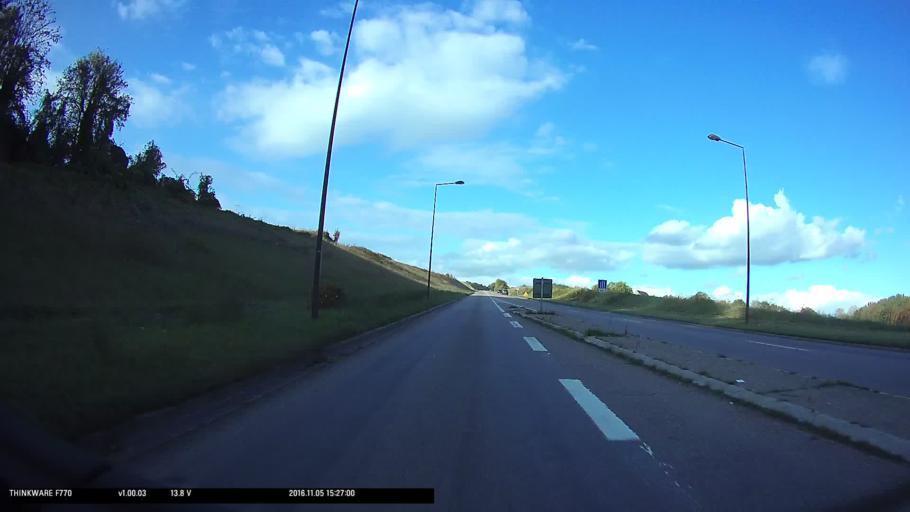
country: FR
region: Ile-de-France
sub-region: Departement des Yvelines
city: Meulan-en-Yvelines
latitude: 49.0167
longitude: 1.9102
